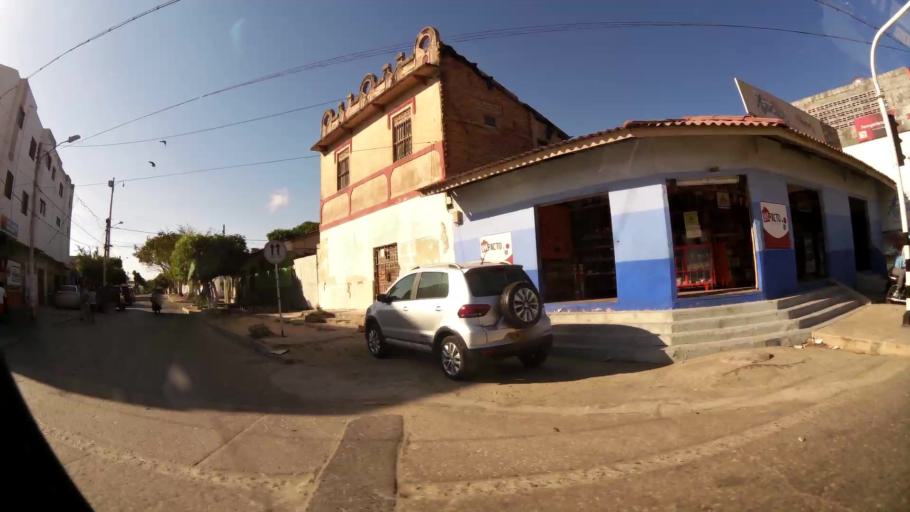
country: CO
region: Atlantico
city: Barranquilla
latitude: 10.9668
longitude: -74.7891
